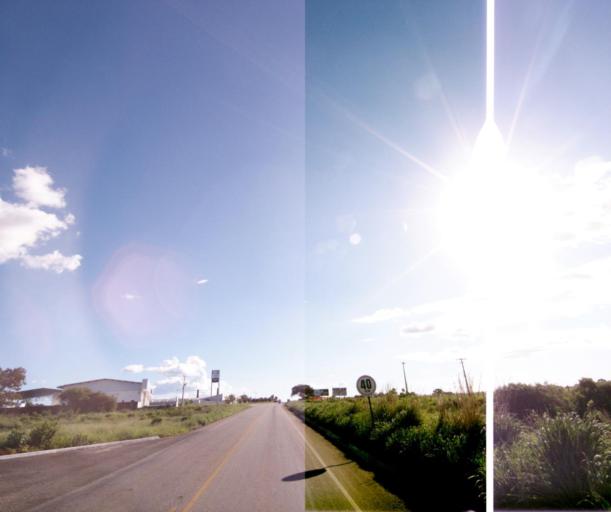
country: BR
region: Bahia
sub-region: Guanambi
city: Guanambi
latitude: -14.1886
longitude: -42.7414
